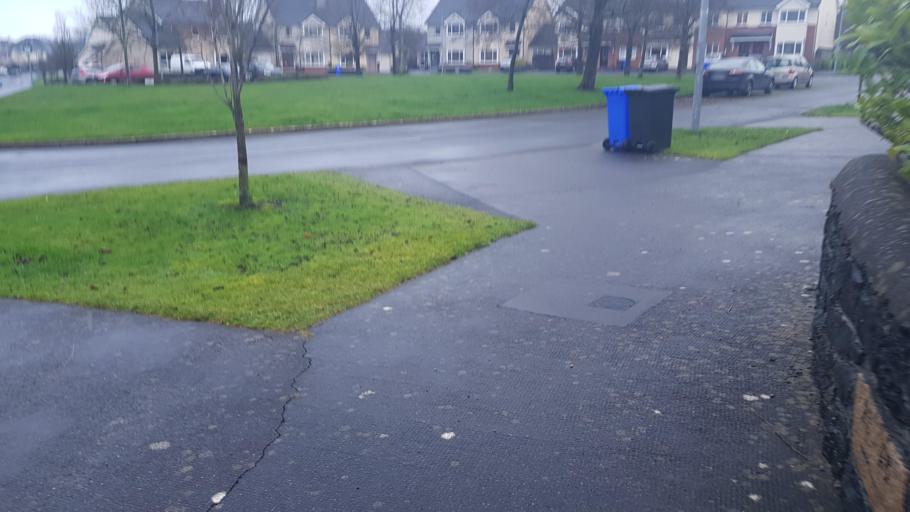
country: IE
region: Connaught
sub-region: County Galway
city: Tuam
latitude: 53.5230
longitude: -8.8488
